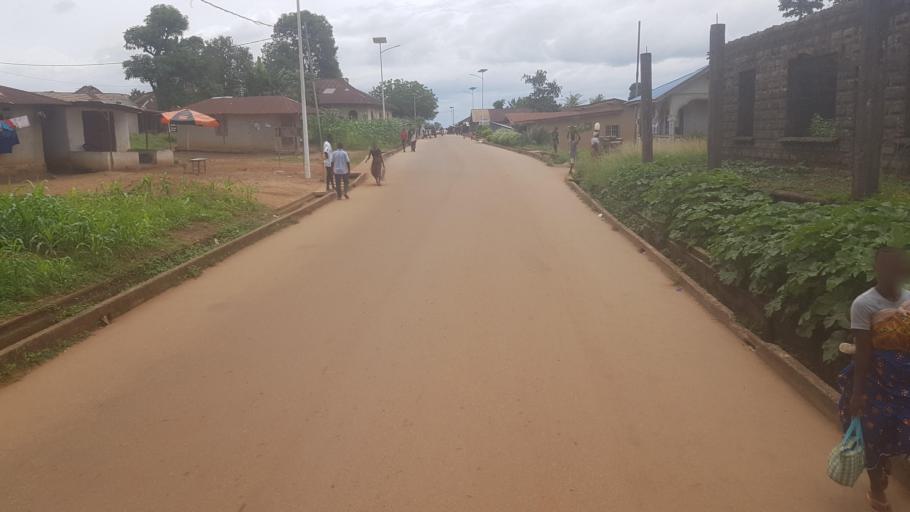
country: SL
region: Southern Province
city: Mogbwemo
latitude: 7.6069
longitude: -12.1806
